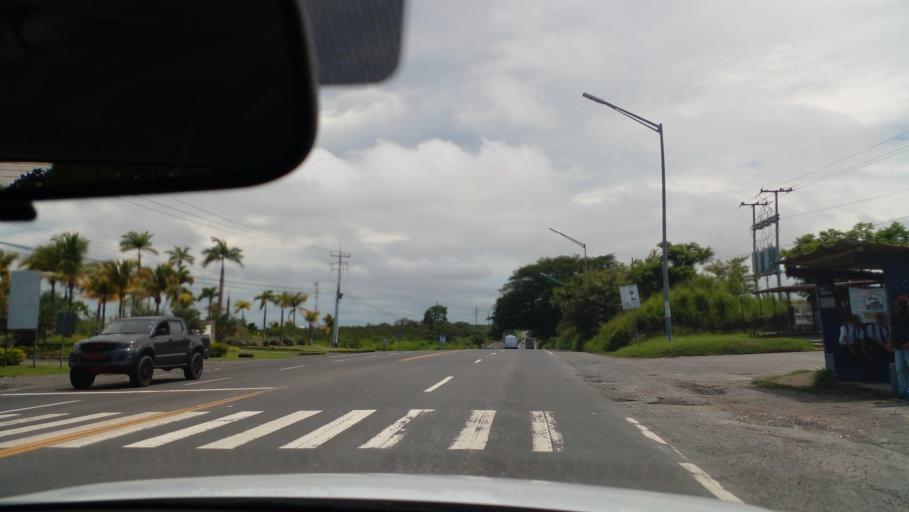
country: PA
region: Panama
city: Nueva Gorgona
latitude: 8.4670
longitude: -79.9661
